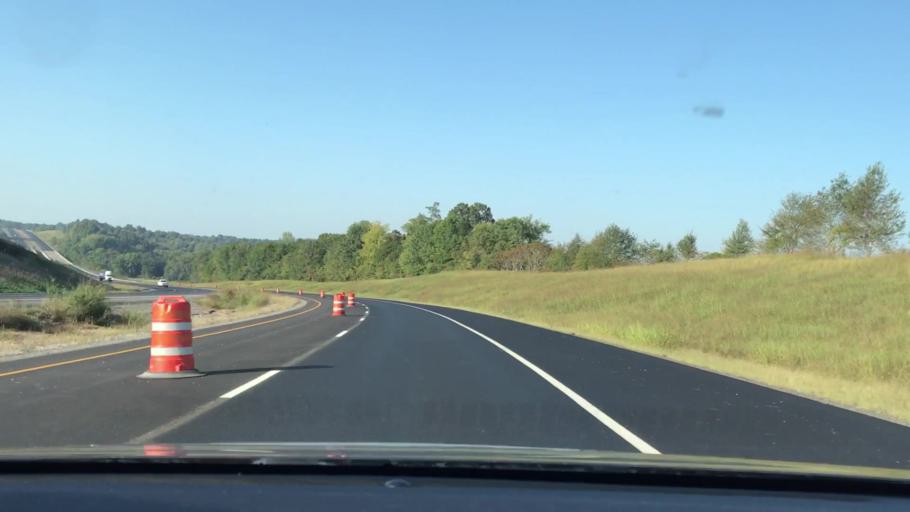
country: US
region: Kentucky
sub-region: Trigg County
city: Cadiz
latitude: 36.8595
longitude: -87.8110
